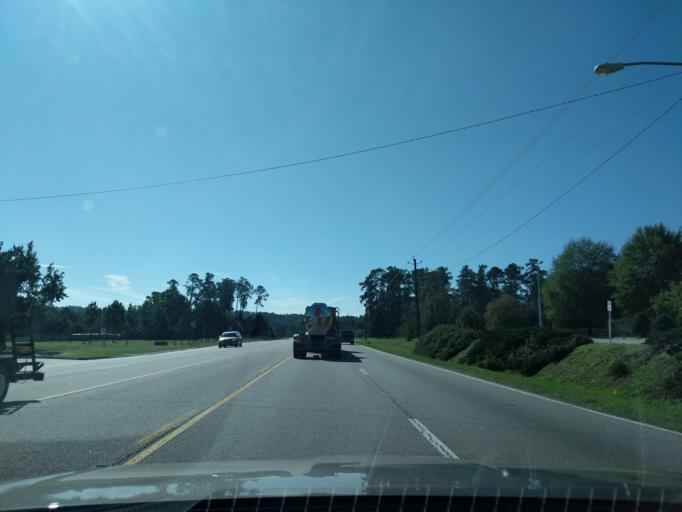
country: US
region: Georgia
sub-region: Richmond County
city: Augusta
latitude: 33.3899
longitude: -82.0050
